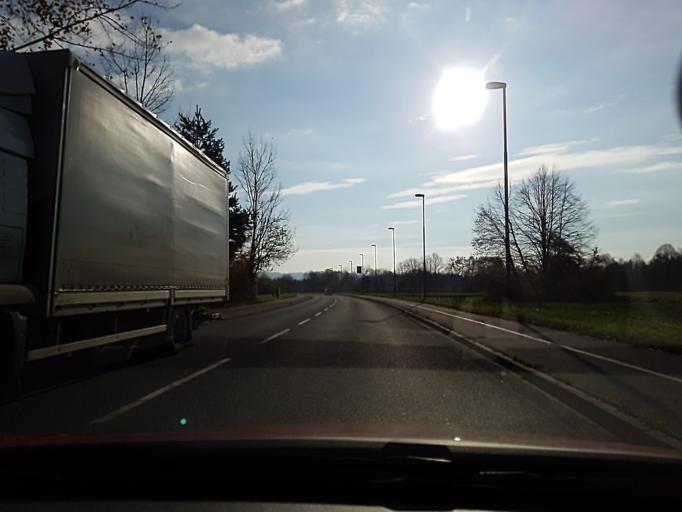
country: SI
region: Trzin
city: Trzin
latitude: 46.0950
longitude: 14.5491
